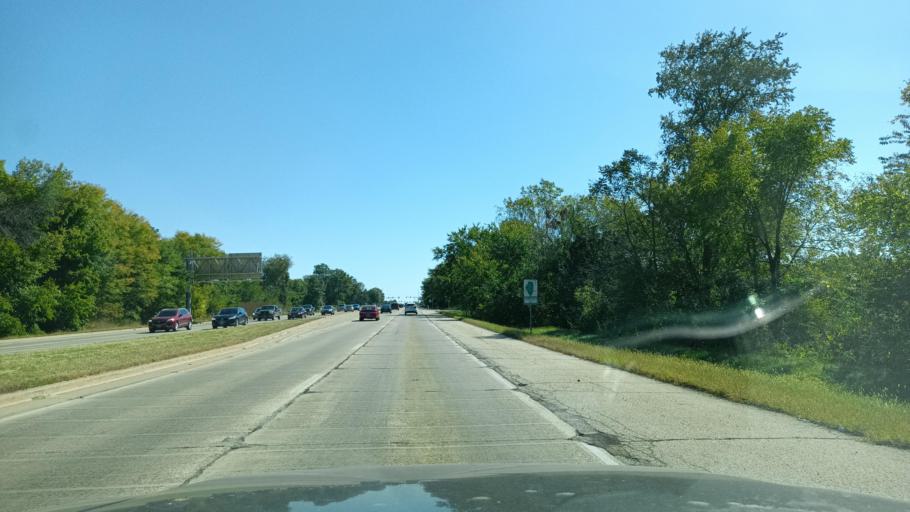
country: US
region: Illinois
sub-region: Peoria County
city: Dunlap
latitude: 40.7741
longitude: -89.6670
